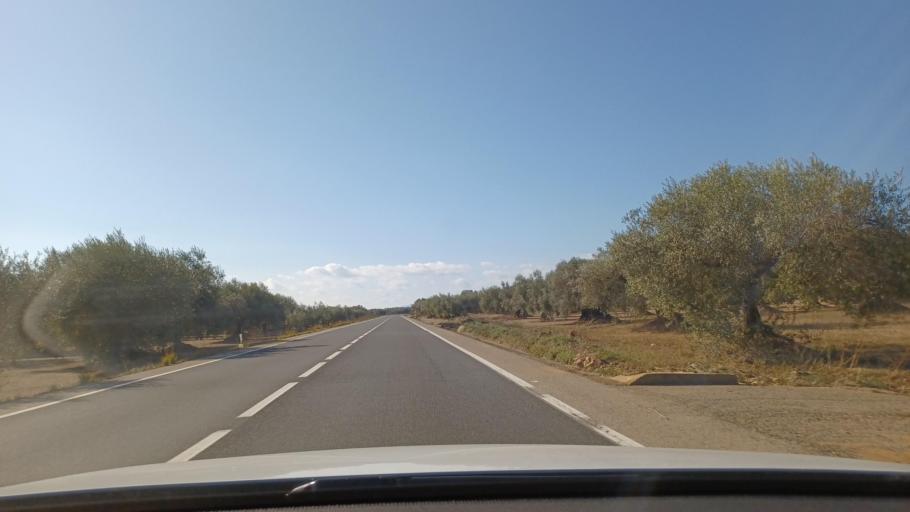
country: ES
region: Catalonia
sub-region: Provincia de Tarragona
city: Ulldecona
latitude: 40.6459
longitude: 0.3832
